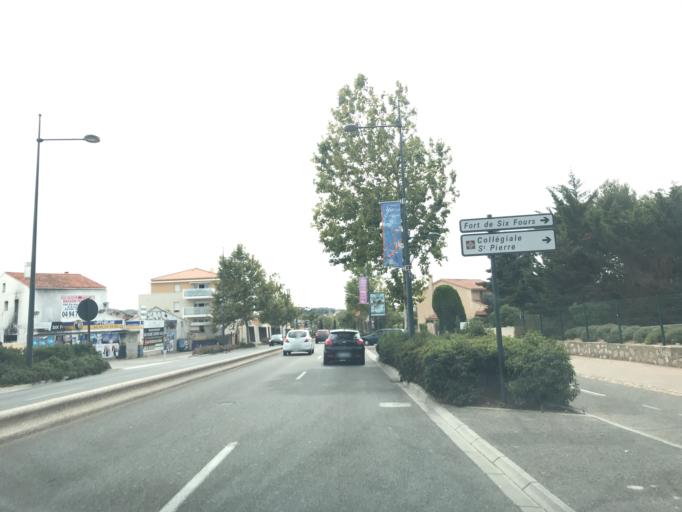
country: FR
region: Provence-Alpes-Cote d'Azur
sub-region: Departement du Var
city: Six-Fours-les-Plages
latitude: 43.0965
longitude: 5.8496
